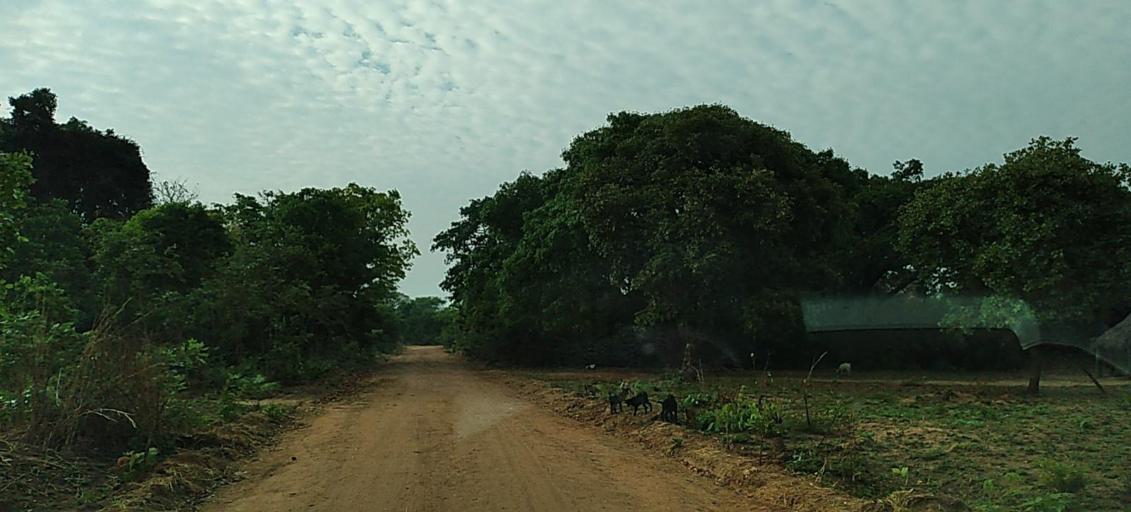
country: ZM
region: Copperbelt
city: Kalulushi
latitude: -12.9070
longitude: 27.6885
